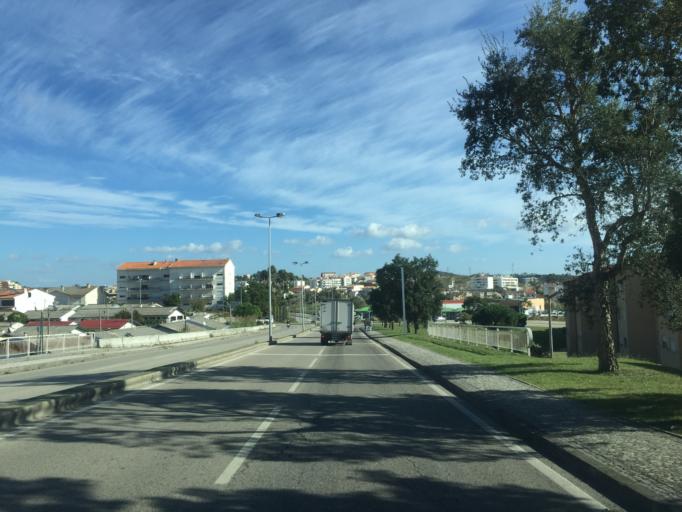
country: PT
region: Coimbra
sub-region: Figueira da Foz
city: Tavarede
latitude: 40.1641
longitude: -8.8499
